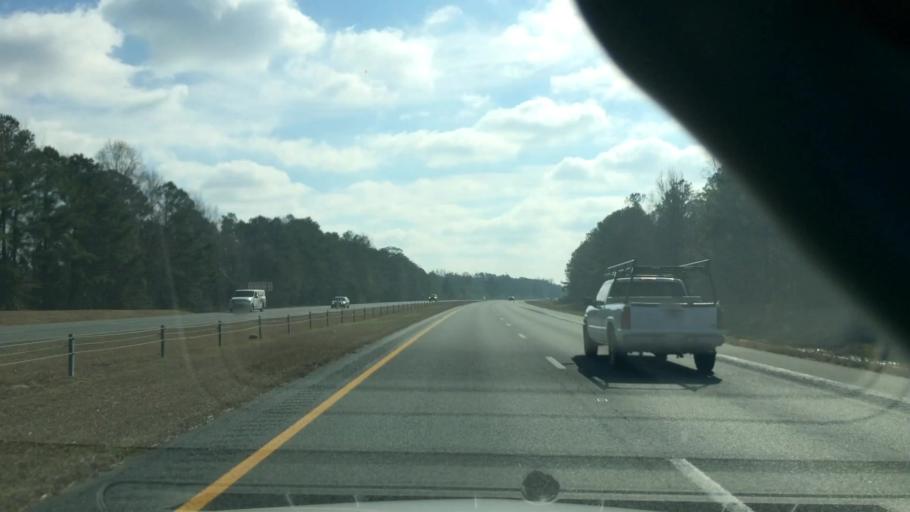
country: US
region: North Carolina
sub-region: Duplin County
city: Wallace
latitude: 34.7005
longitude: -77.9450
